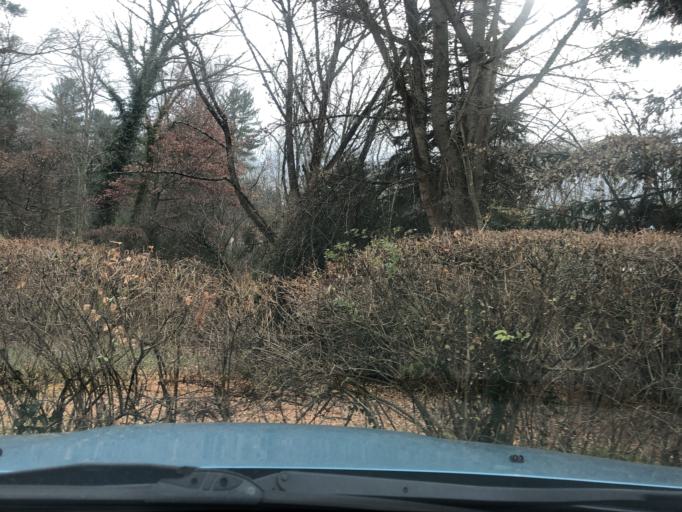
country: US
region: Pennsylvania
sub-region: Delaware County
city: Radnor
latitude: 40.0275
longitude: -75.3579
